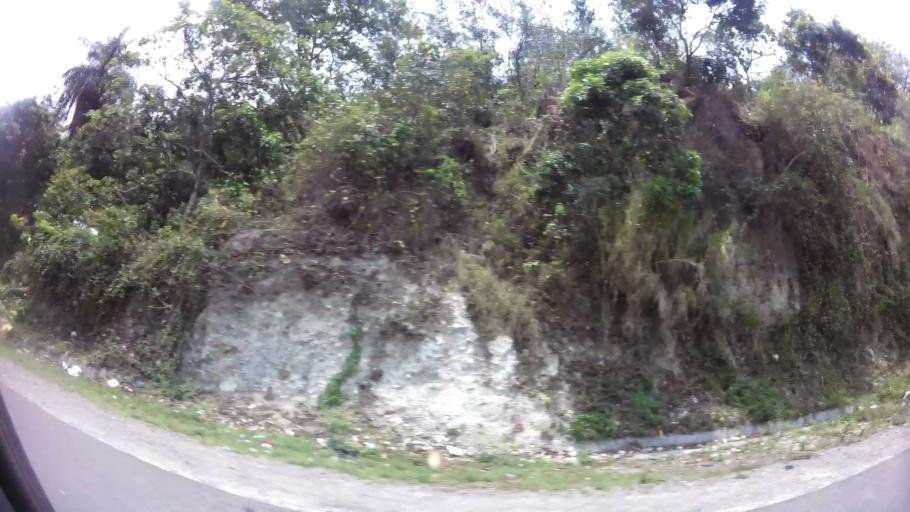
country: HN
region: Comayagua
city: Taulabe
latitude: 14.6853
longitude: -87.9495
